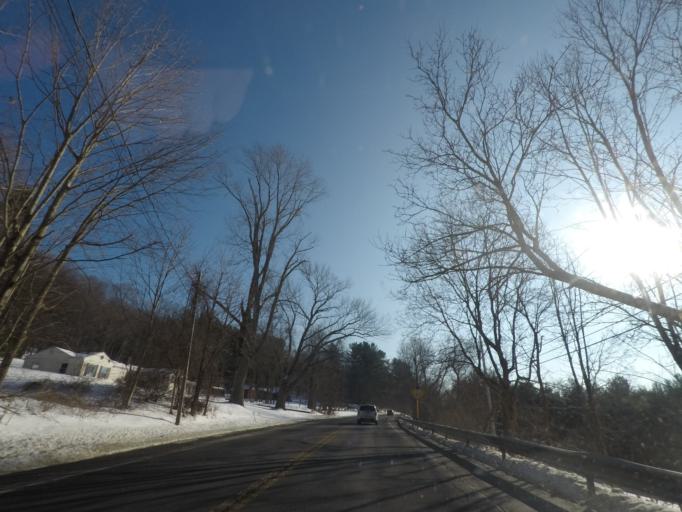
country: US
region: Massachusetts
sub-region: Berkshire County
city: Richmond
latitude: 42.4878
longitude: -73.3731
